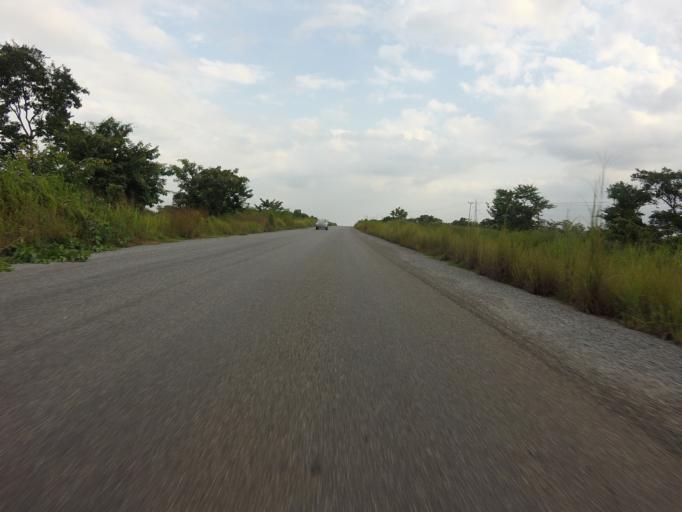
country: GH
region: Volta
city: Ho
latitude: 6.4147
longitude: 0.5211
